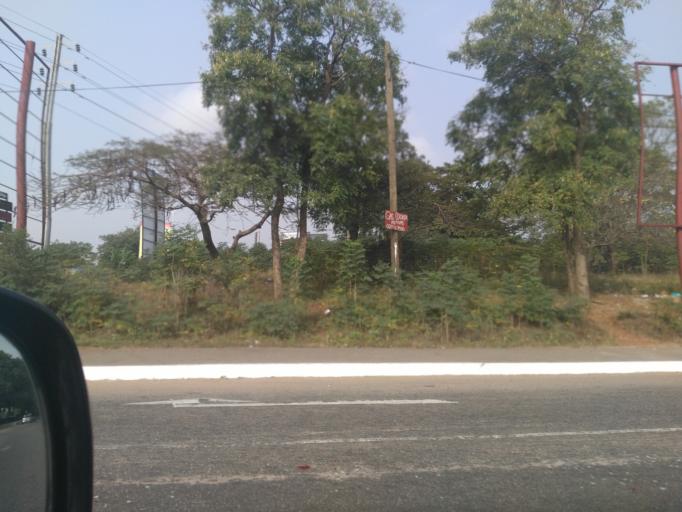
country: GH
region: Greater Accra
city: Accra
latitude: 5.5960
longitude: -0.1893
